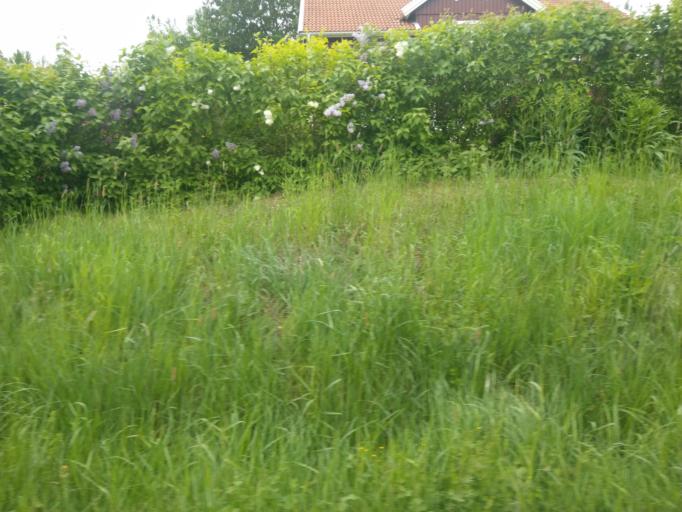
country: SE
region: Stockholm
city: Stenhamra
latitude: 59.4089
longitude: 17.6231
